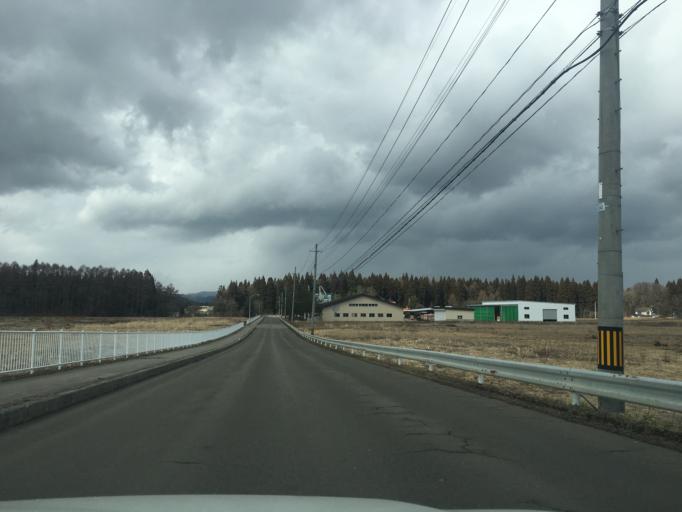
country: JP
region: Akita
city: Takanosu
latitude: 40.1835
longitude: 140.3417
